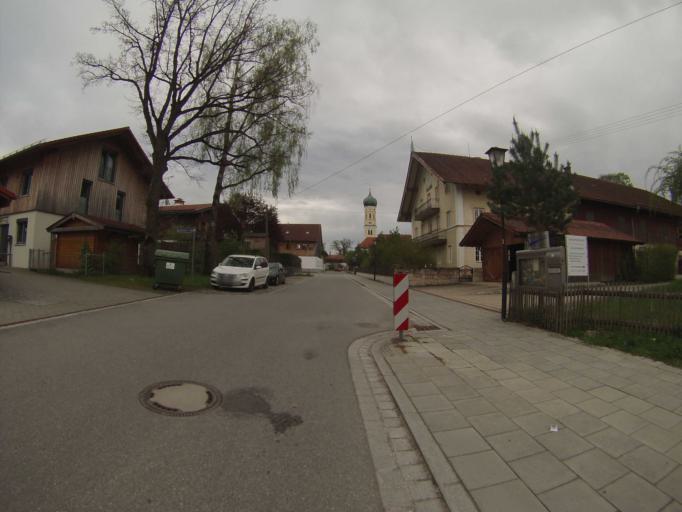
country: DE
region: Bavaria
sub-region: Upper Bavaria
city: Sauerlach
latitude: 47.9734
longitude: 11.6499
